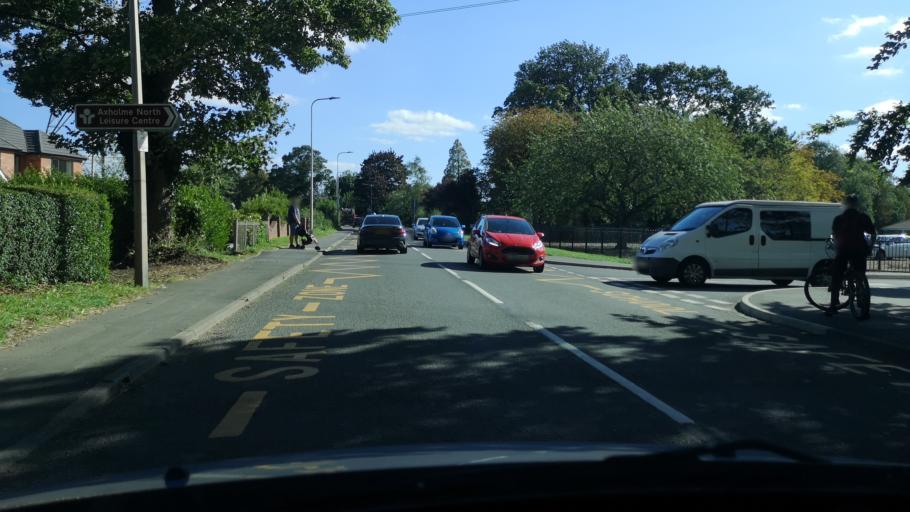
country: GB
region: England
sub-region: North Lincolnshire
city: Crowle
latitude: 53.6004
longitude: -0.8274
